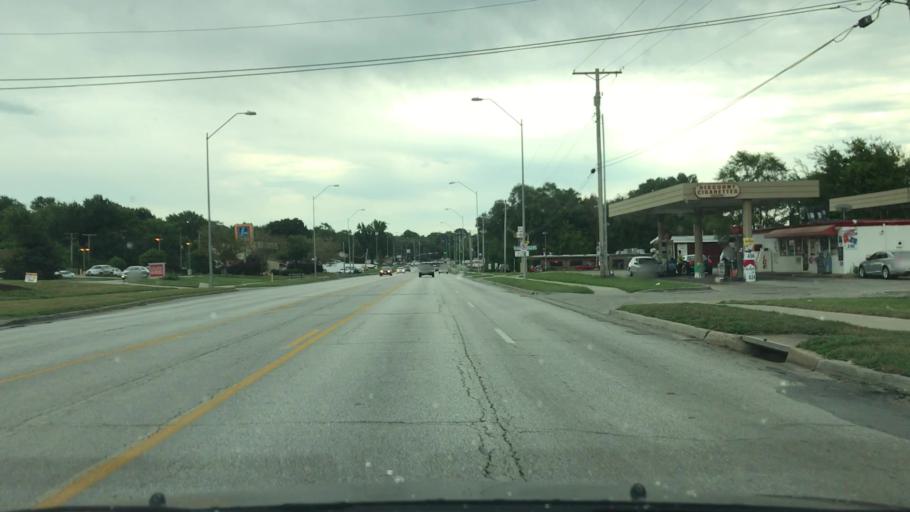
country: US
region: Missouri
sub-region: Jackson County
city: Grandview
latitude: 38.9355
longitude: -94.5084
